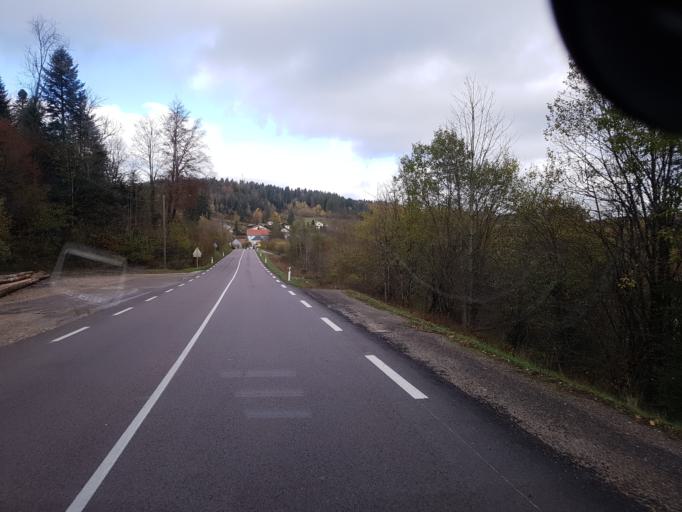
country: FR
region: Franche-Comte
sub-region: Departement du Jura
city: Champagnole
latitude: 46.6509
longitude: 5.9423
